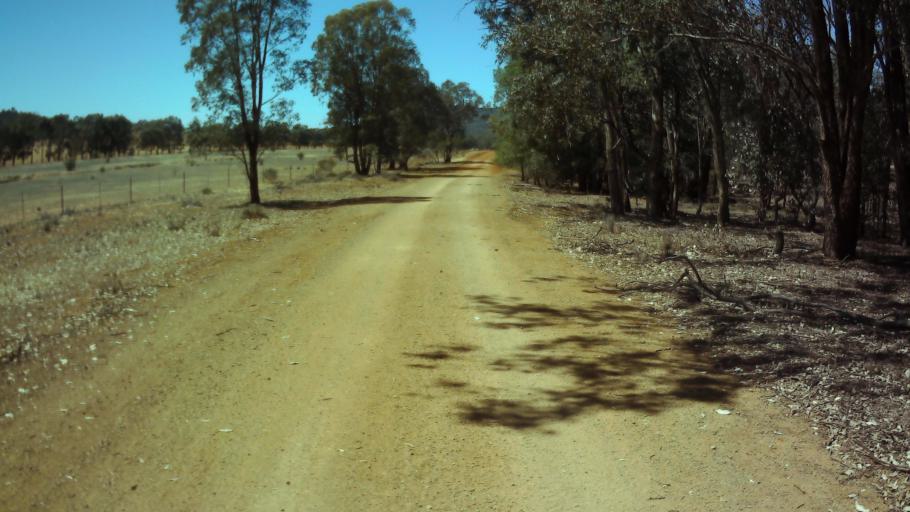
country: AU
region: New South Wales
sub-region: Weddin
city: Grenfell
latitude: -33.9491
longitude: 148.0843
